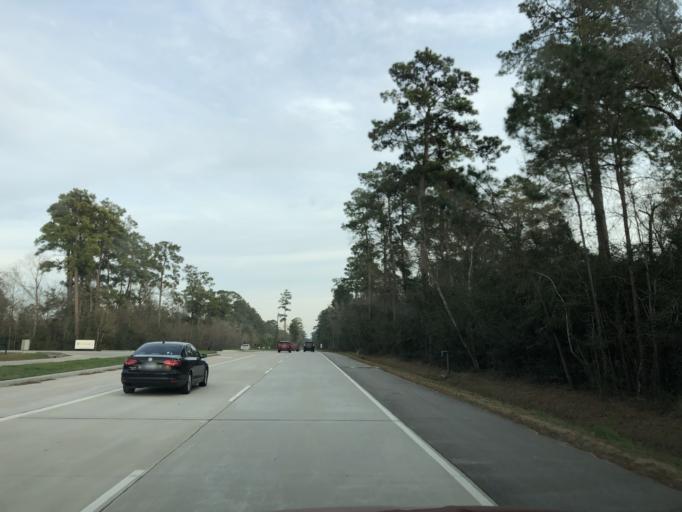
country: US
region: Texas
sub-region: Montgomery County
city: The Woodlands
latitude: 30.2156
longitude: -95.5579
